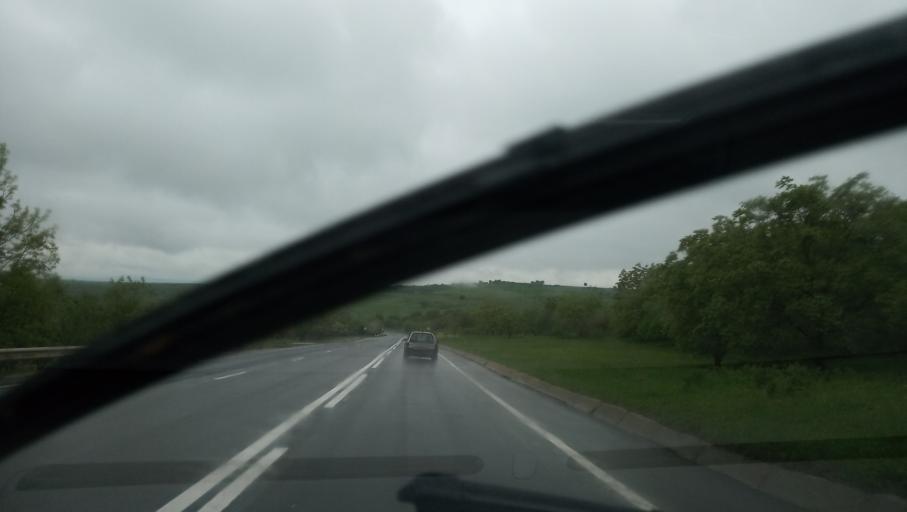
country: RO
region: Sibiu
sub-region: Comuna Tilisca
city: Tilisca
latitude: 45.8297
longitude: 23.8572
